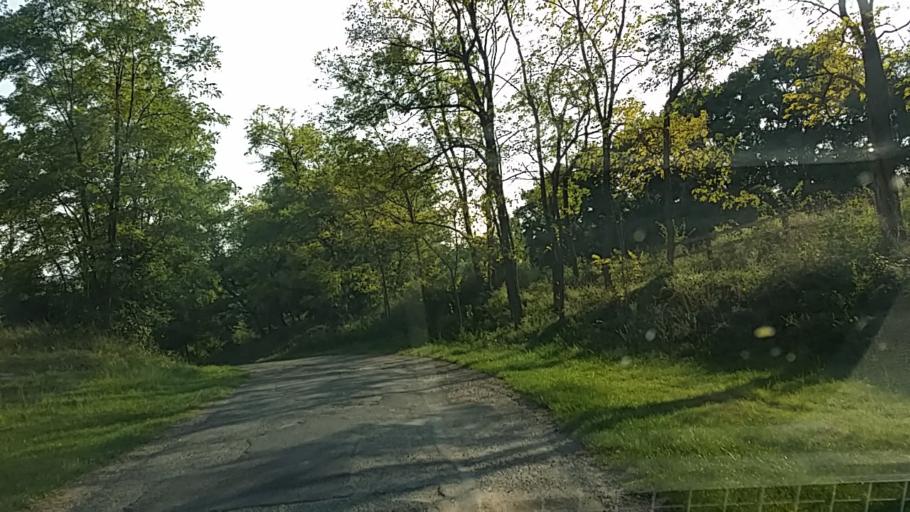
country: HU
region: Nograd
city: Bujak
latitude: 47.8704
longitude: 19.5007
